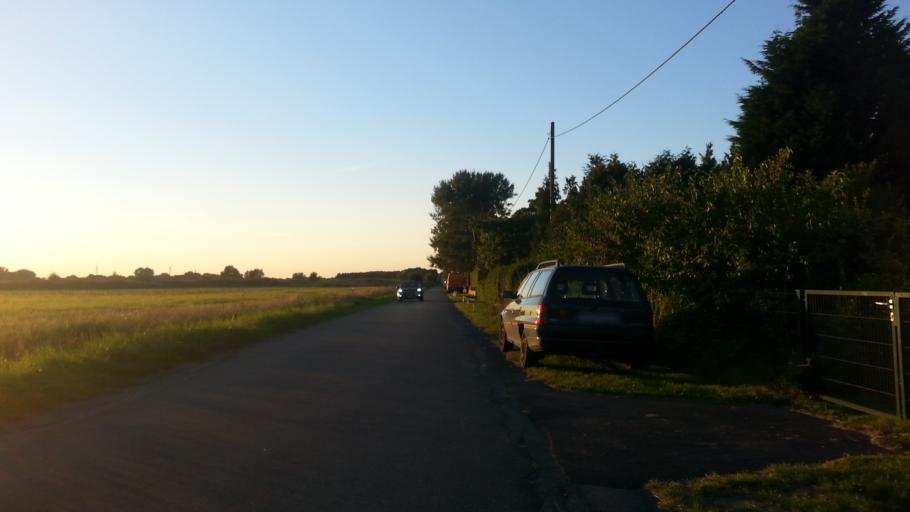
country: DE
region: North Rhine-Westphalia
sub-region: Regierungsbezirk Munster
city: Muenster
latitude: 52.0300
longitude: 7.6558
